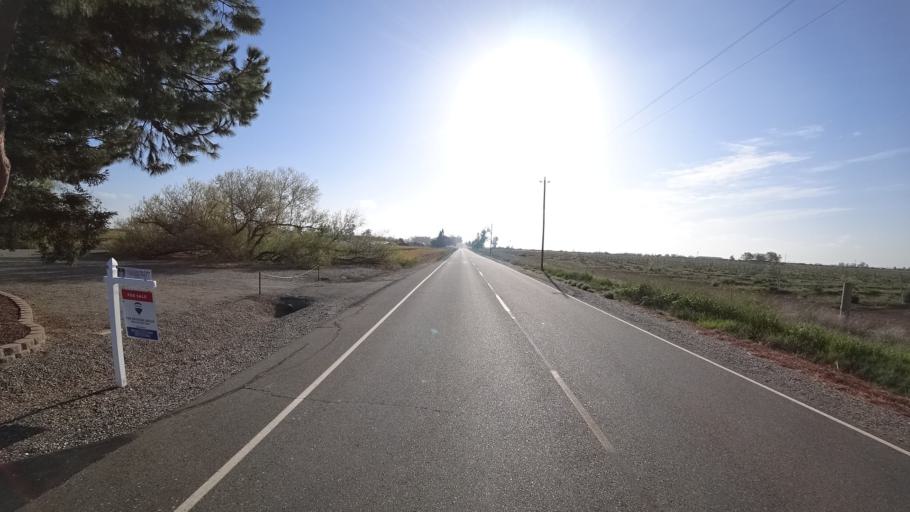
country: US
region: California
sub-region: Glenn County
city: Willows
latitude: 39.5825
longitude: -122.2166
